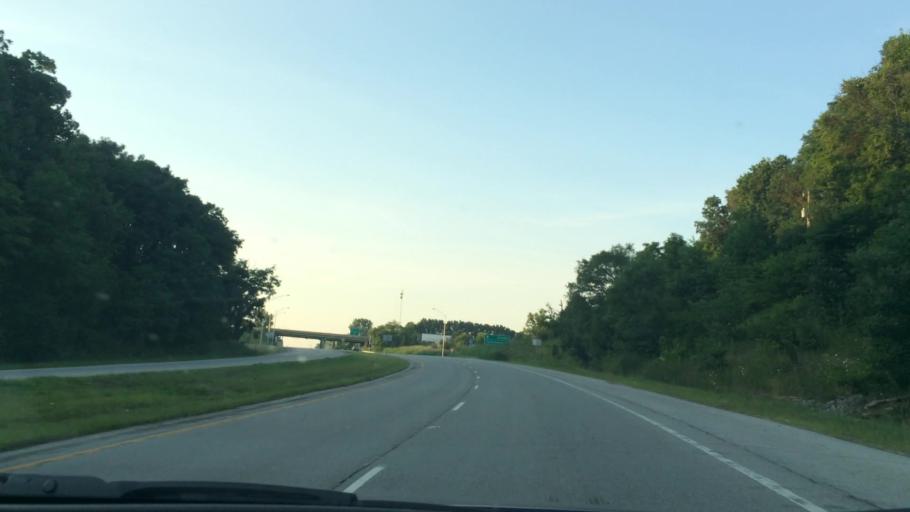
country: US
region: Indiana
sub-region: Tippecanoe County
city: Battle Ground
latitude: 40.4935
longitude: -86.8685
